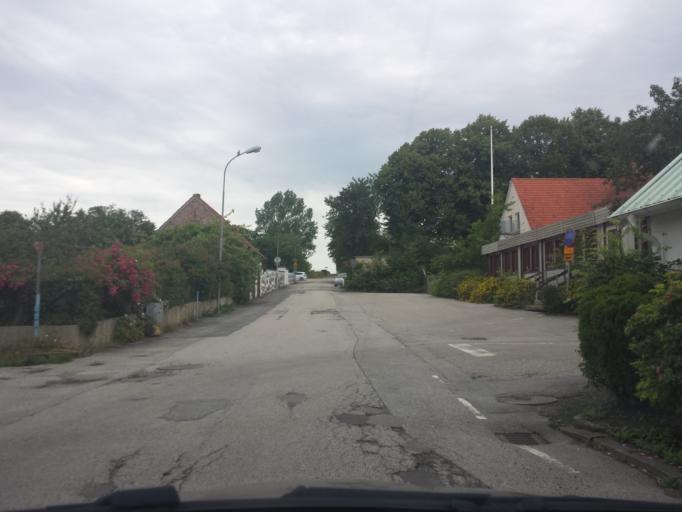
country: SE
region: Skane
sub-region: Ystads Kommun
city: Kopingebro
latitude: 55.4549
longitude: 14.0201
